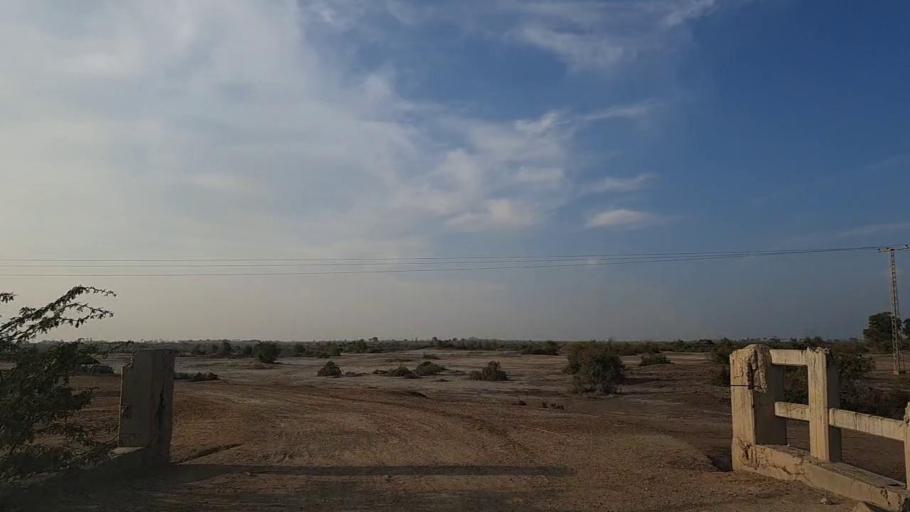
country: PK
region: Sindh
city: Bandhi
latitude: 26.5649
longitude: 68.2465
